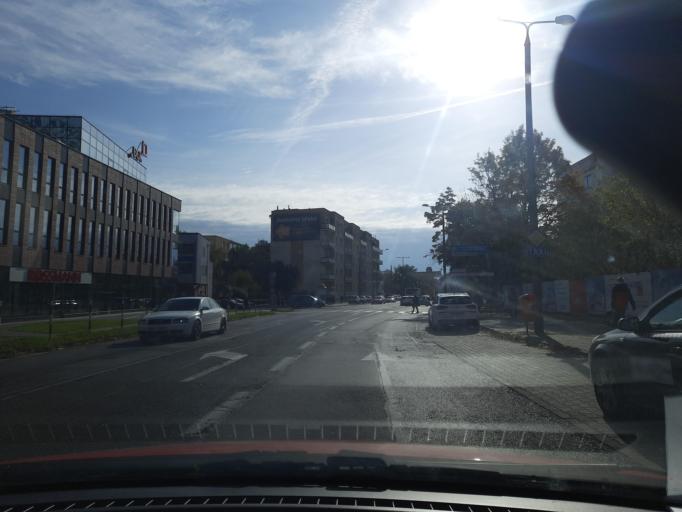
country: PL
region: Kujawsko-Pomorskie
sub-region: Torun
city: Torun
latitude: 53.0169
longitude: 18.6015
